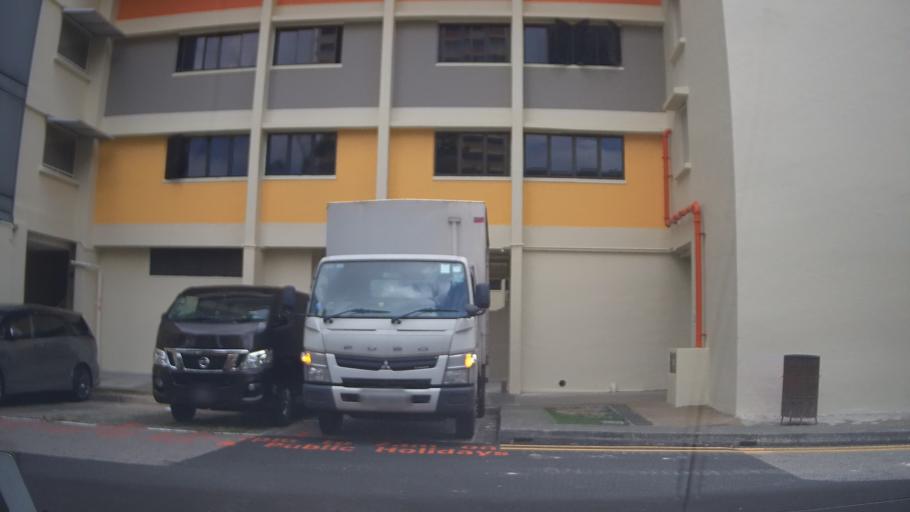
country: SG
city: Singapore
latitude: 1.3025
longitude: 103.7626
